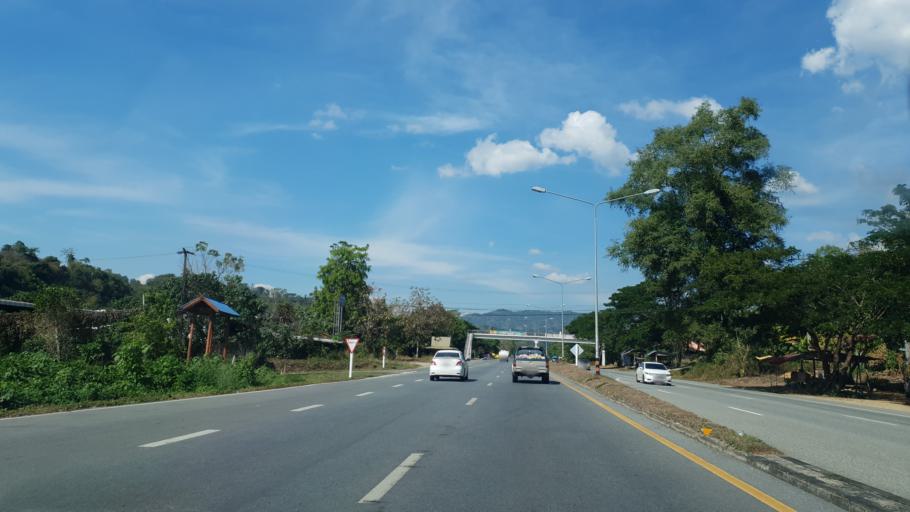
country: TH
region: Uttaradit
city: Lap Lae
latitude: 17.7878
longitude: 100.1178
